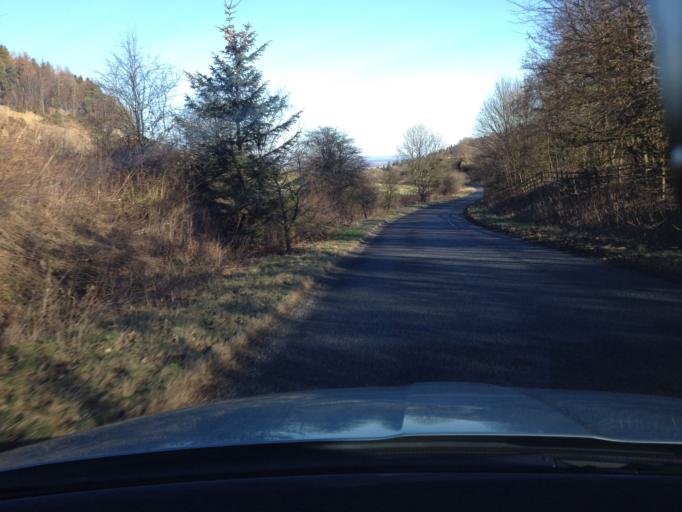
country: GB
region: Scotland
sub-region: Perth and Kinross
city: Bridge of Earn
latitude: 56.3097
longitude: -3.3824
